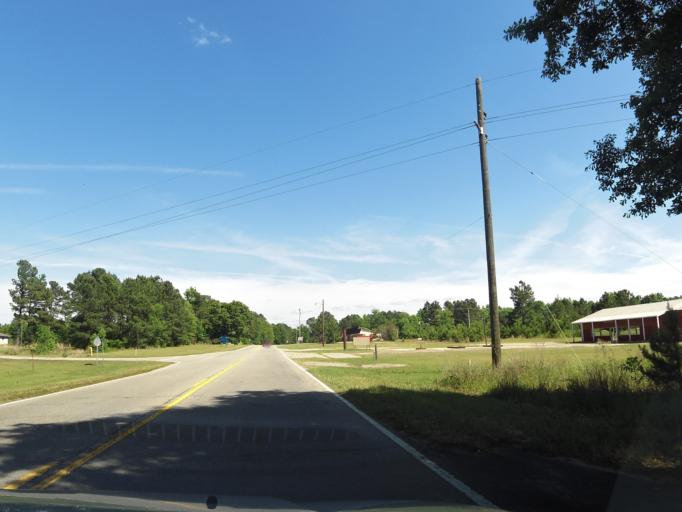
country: US
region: South Carolina
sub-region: Barnwell County
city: Williston
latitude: 33.3918
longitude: -81.4026
